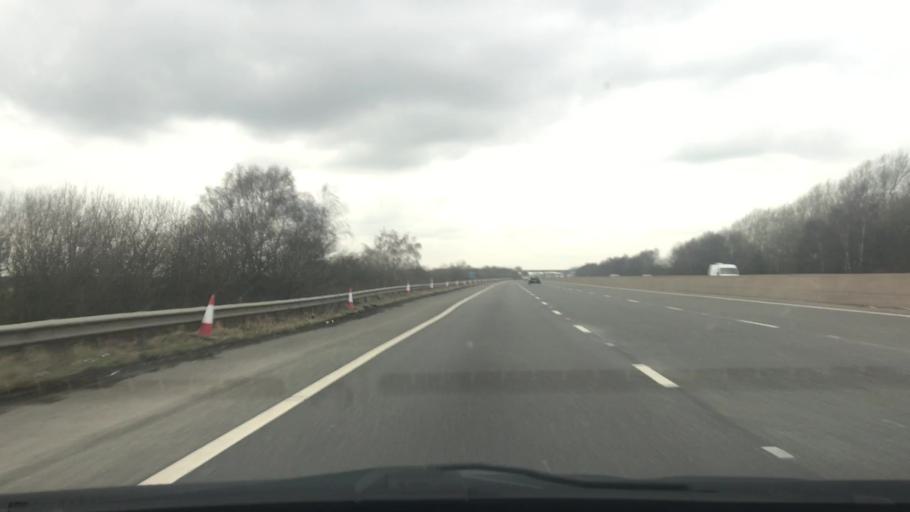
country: GB
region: England
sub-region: North Lincolnshire
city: Crowle
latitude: 53.5738
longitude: -0.9105
